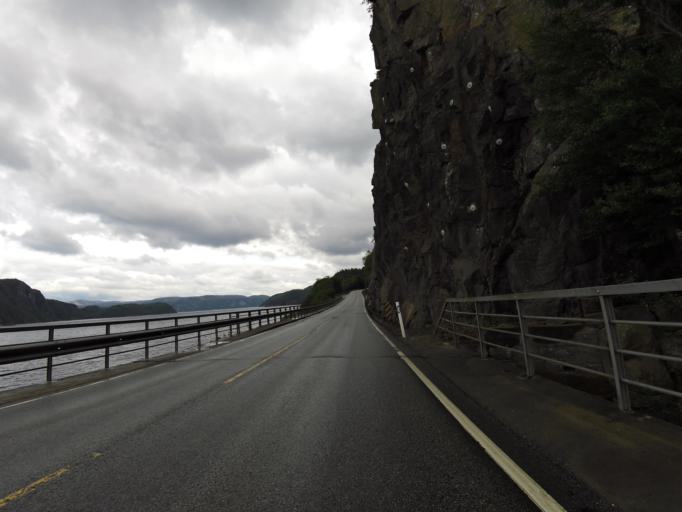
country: NO
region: Vest-Agder
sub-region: Farsund
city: Farsund
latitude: 58.0985
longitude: 6.8197
